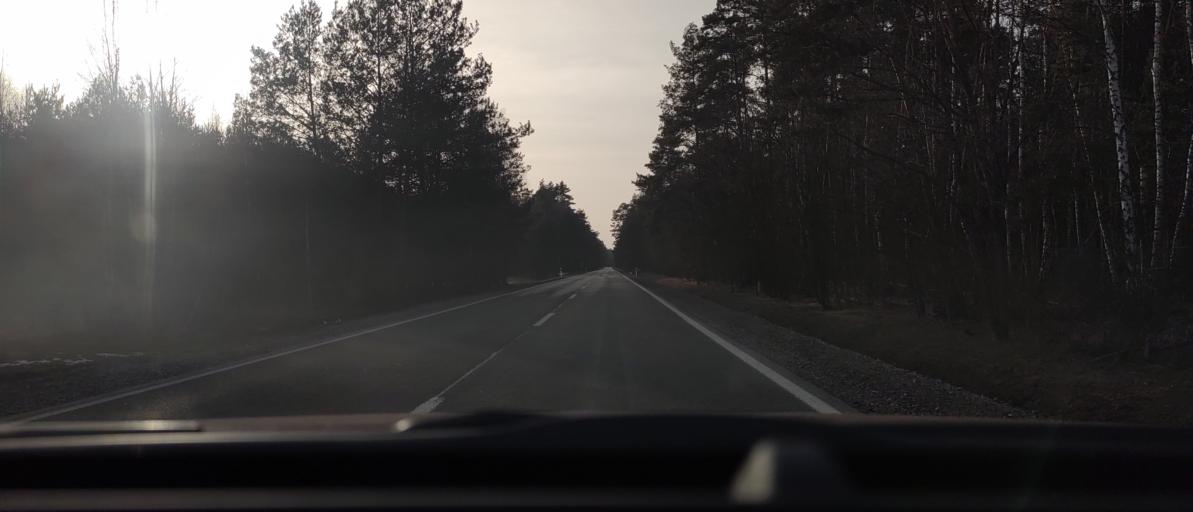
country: PL
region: Masovian Voivodeship
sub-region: Powiat bialobrzeski
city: Wysmierzyce
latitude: 51.6281
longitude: 20.8723
